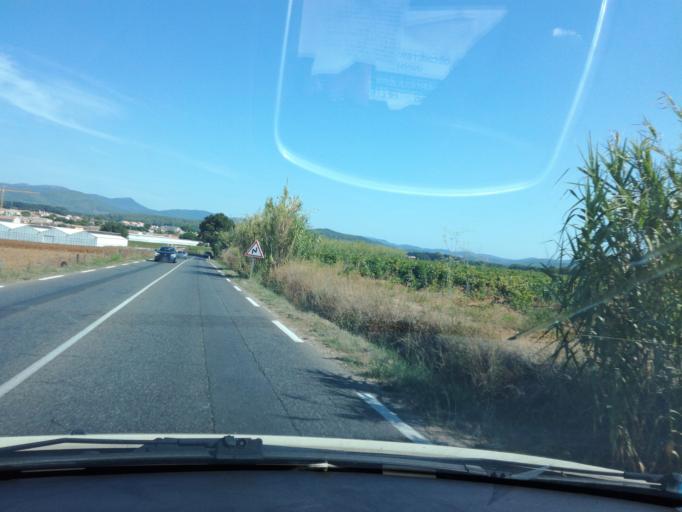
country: FR
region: Provence-Alpes-Cote d'Azur
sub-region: Departement du Var
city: La Crau
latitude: 43.1370
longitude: 6.0796
